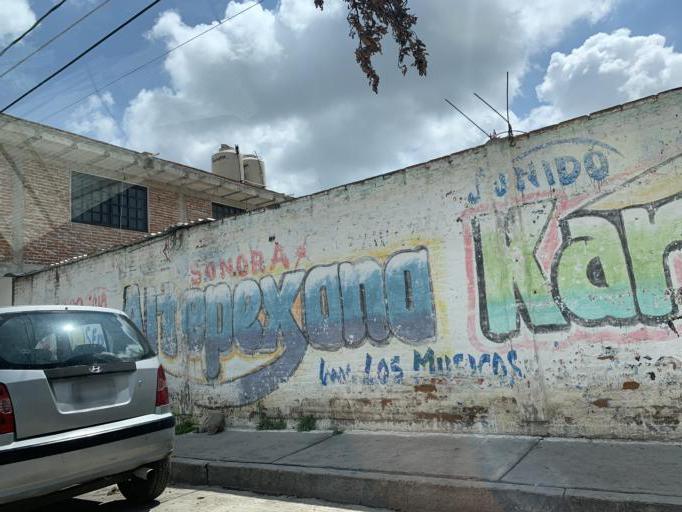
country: MX
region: Puebla
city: Huejotzingo
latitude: 19.1560
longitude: -98.4110
